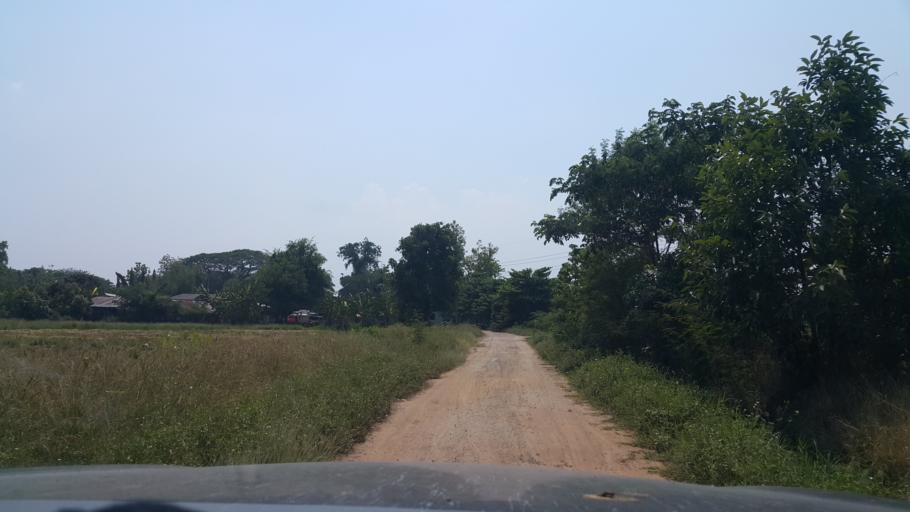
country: TH
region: Chiang Mai
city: Saraphi
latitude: 18.7217
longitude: 98.9757
